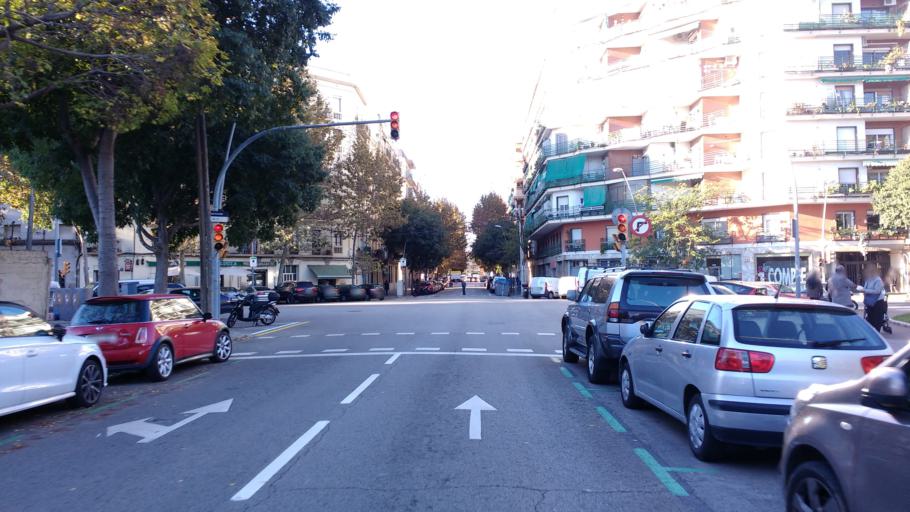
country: ES
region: Catalonia
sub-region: Provincia de Barcelona
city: Sant Marti
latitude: 41.4036
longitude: 2.2078
